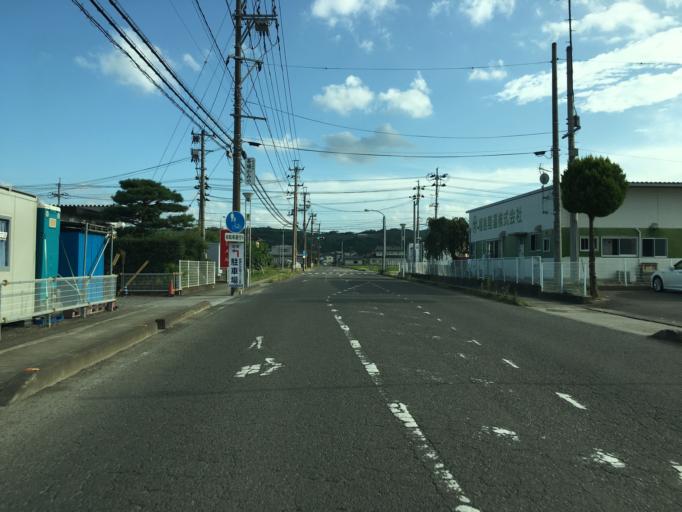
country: JP
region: Fukushima
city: Hobaramachi
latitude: 37.8096
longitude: 140.5516
